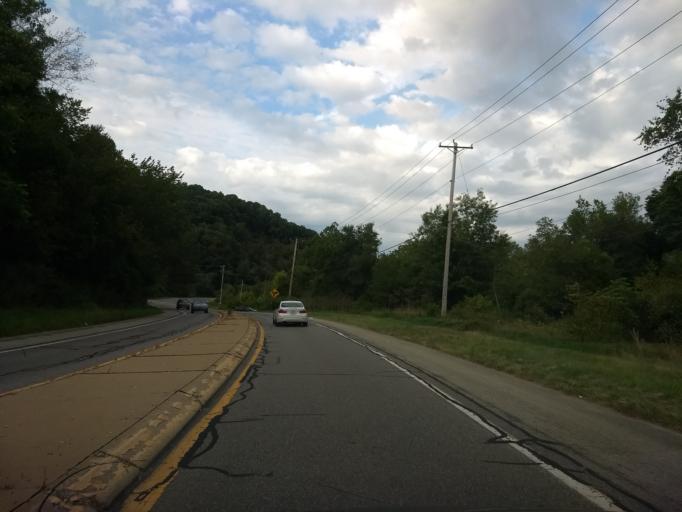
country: US
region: Pennsylvania
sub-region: Allegheny County
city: Coraopolis
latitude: 40.4600
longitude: -80.1696
